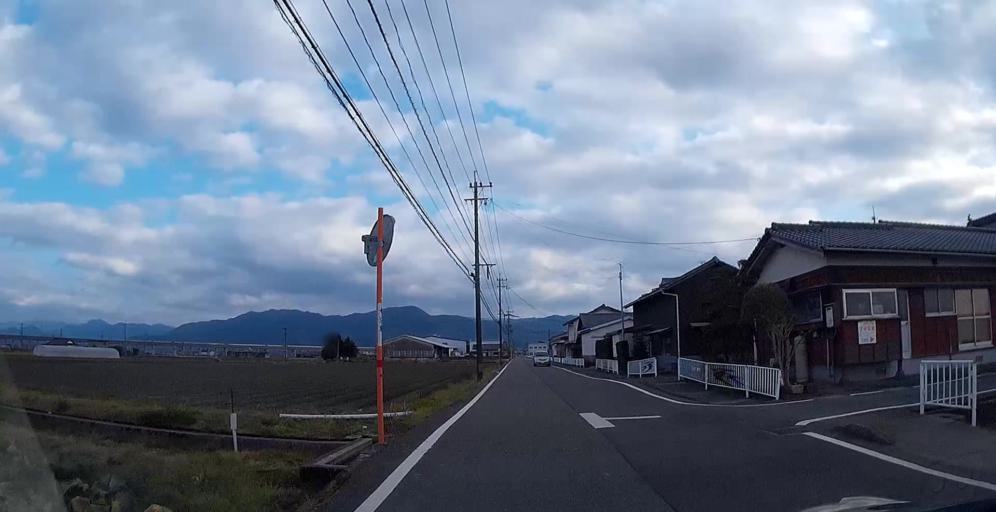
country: JP
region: Kumamoto
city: Yatsushiro
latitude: 32.5456
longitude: 130.6186
